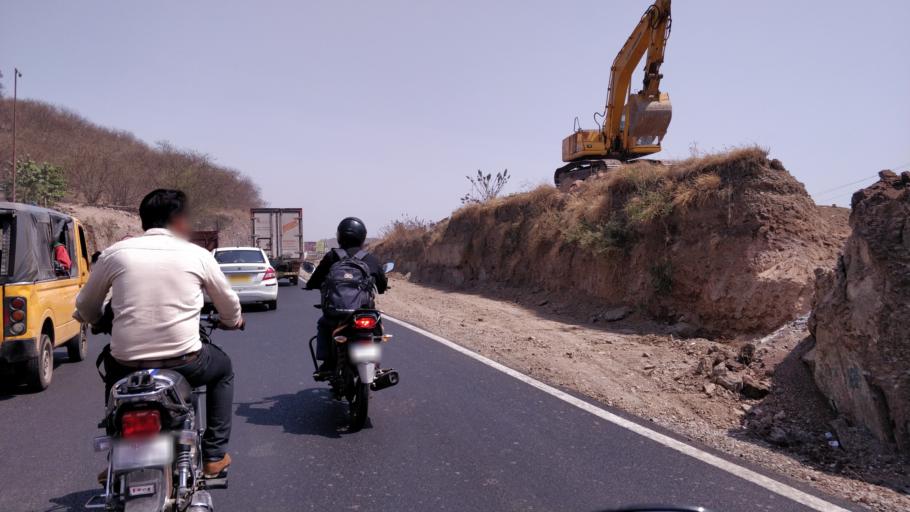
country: IN
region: Maharashtra
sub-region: Pune Division
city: Shivaji Nagar
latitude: 18.5347
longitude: 73.7802
